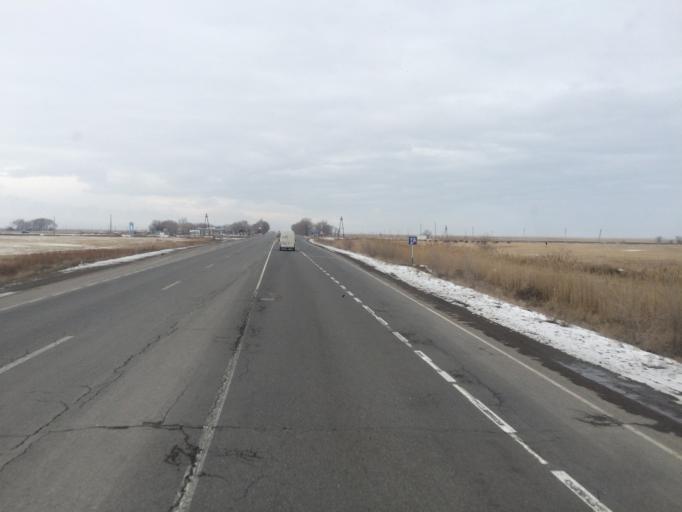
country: KG
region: Chuy
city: Tokmok
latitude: 43.3493
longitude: 75.4838
